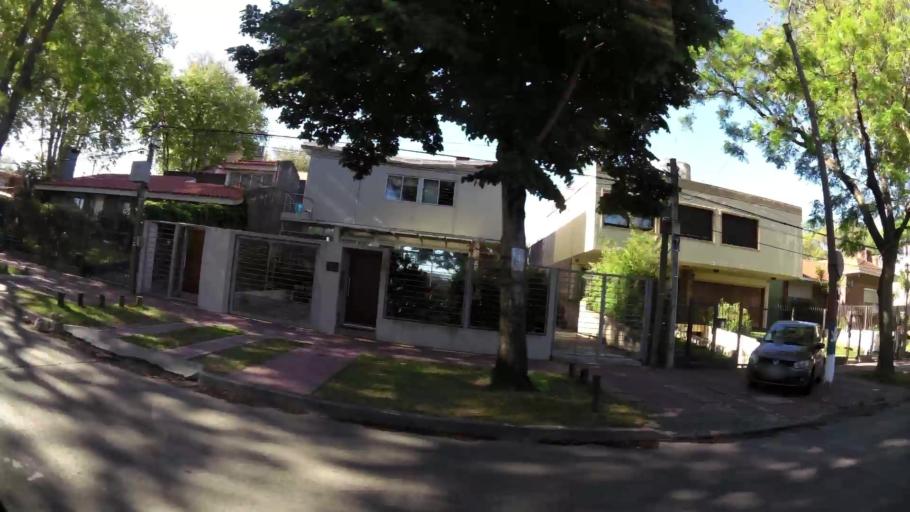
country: UY
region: Canelones
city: Paso de Carrasco
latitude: -34.8907
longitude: -56.0854
